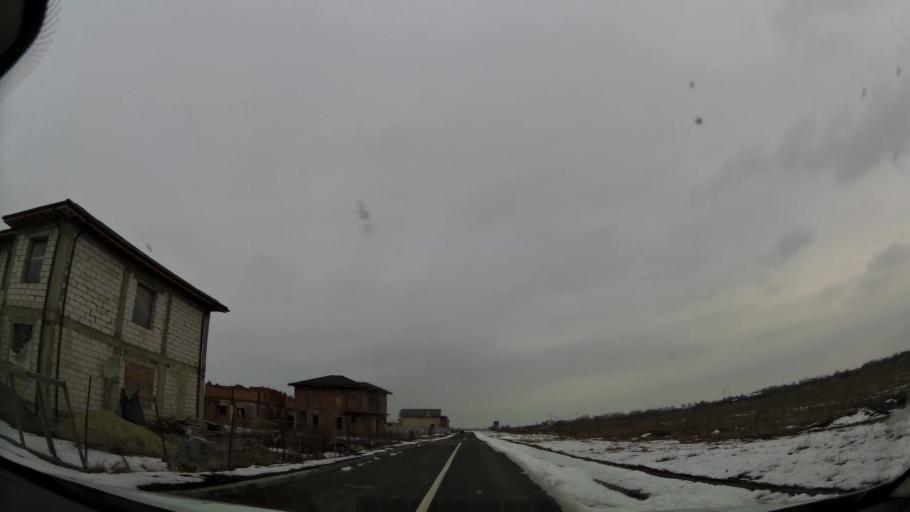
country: RO
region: Ilfov
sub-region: Comuna Tunari
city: Tunari
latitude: 44.5511
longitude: 26.1541
